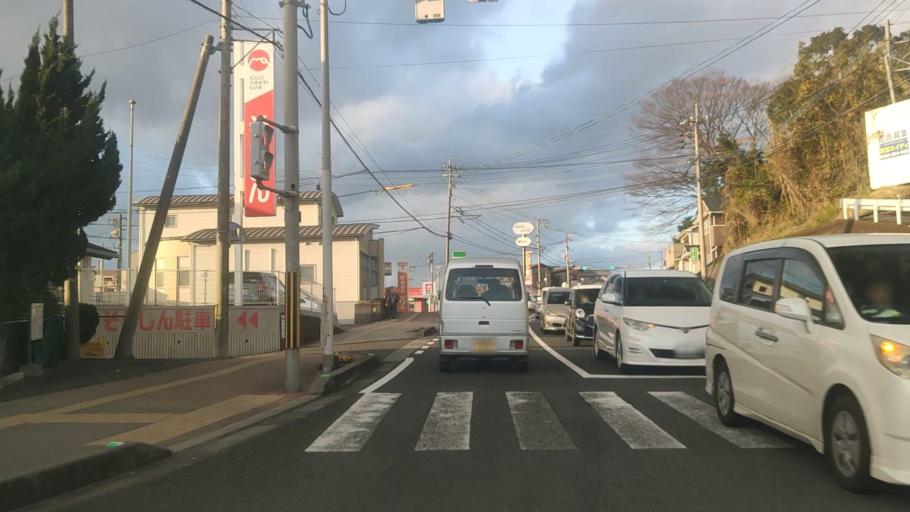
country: JP
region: Kagoshima
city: Kagoshima-shi
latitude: 31.6207
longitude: 130.5531
